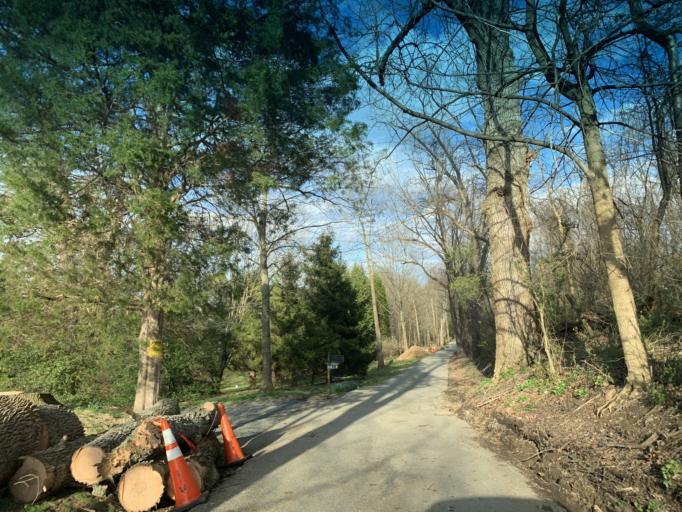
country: US
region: Maryland
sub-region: Harford County
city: South Bel Air
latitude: 39.5736
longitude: -76.2739
